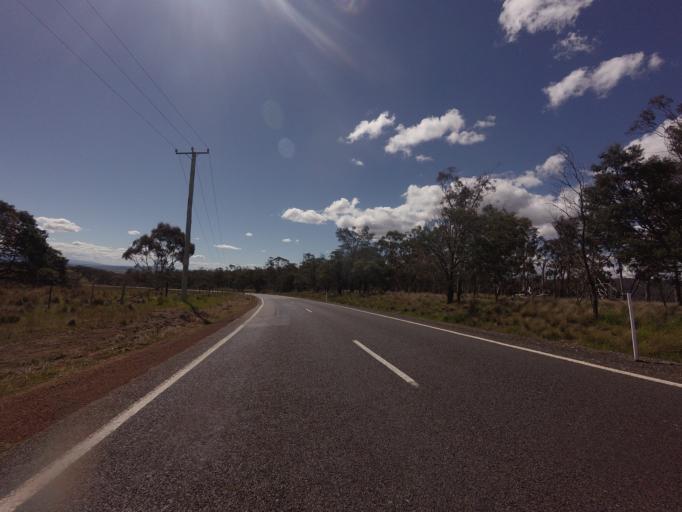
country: AU
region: Tasmania
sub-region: Northern Midlands
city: Evandale
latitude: -41.9424
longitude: 147.6037
